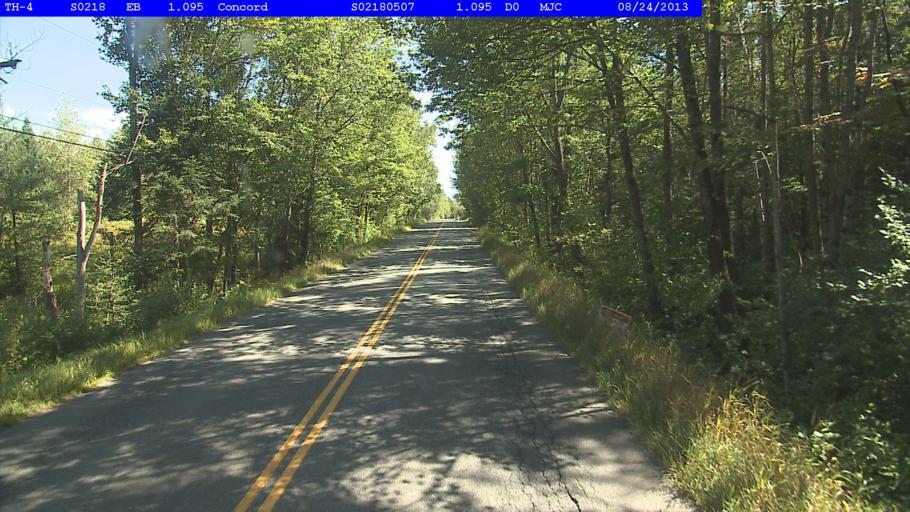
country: US
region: New Hampshire
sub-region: Grafton County
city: Littleton
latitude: 44.4502
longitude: -71.7678
